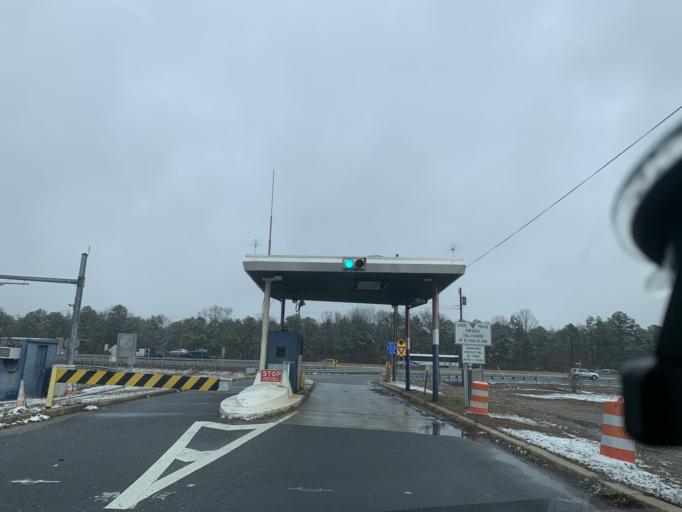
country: US
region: New Jersey
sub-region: Atlantic County
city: Pomona
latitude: 39.4353
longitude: -74.5911
